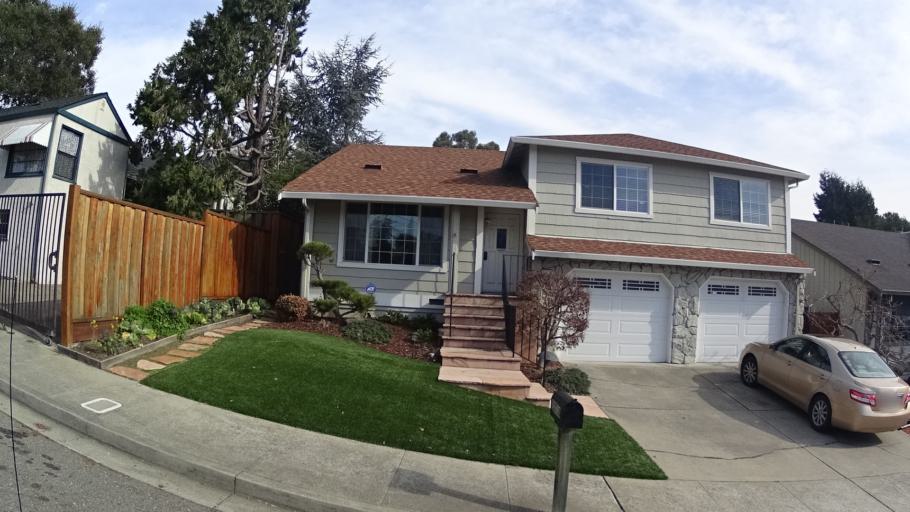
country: US
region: California
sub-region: Alameda County
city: Fairview
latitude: 37.6789
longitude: -122.0598
